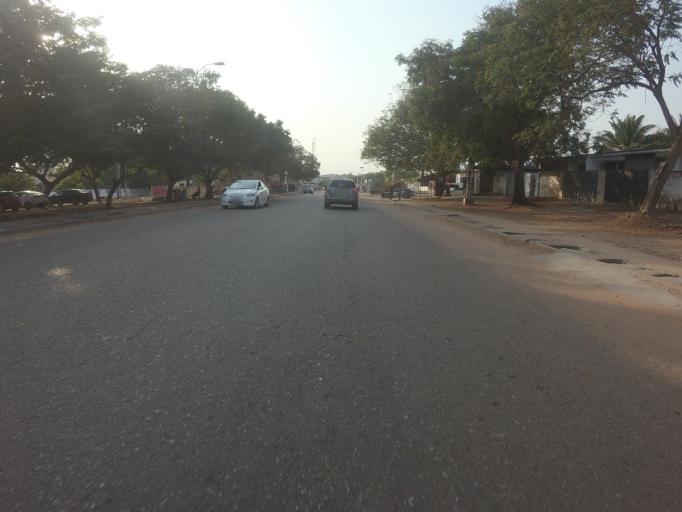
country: GH
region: Greater Accra
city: Nungua
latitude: 5.6231
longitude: -0.0601
